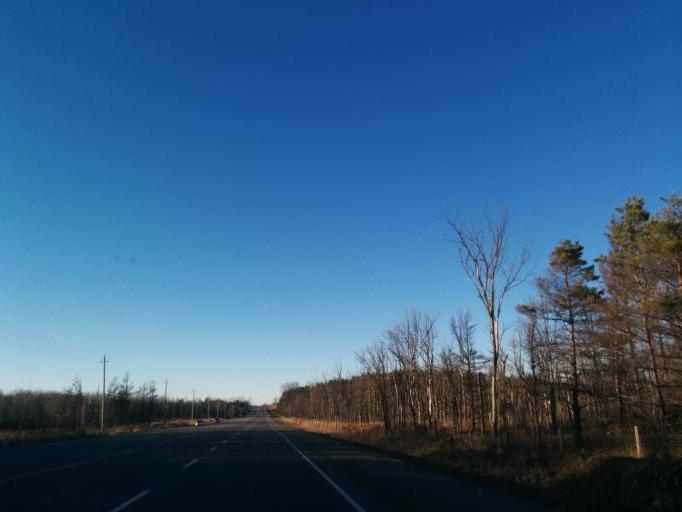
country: CA
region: Ontario
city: Orangeville
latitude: 43.9056
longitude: -80.0576
